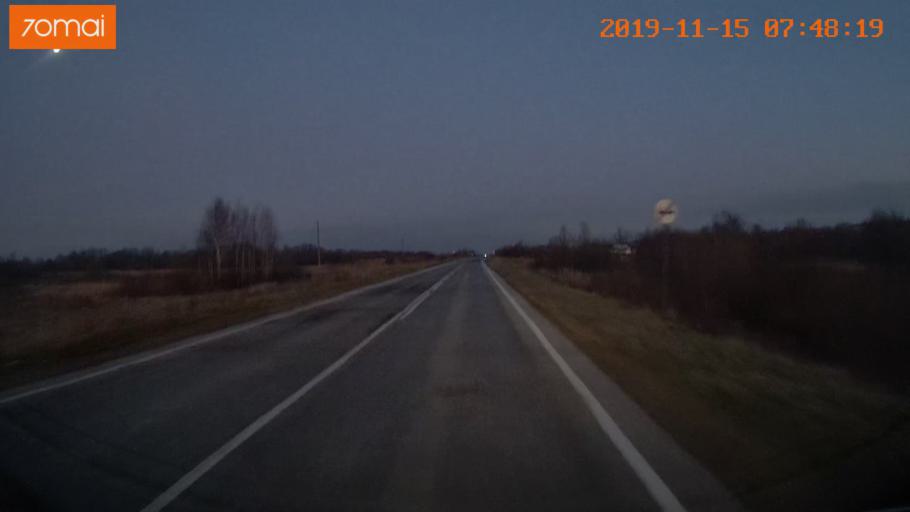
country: RU
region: Vologda
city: Sheksna
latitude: 58.8468
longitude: 38.2507
